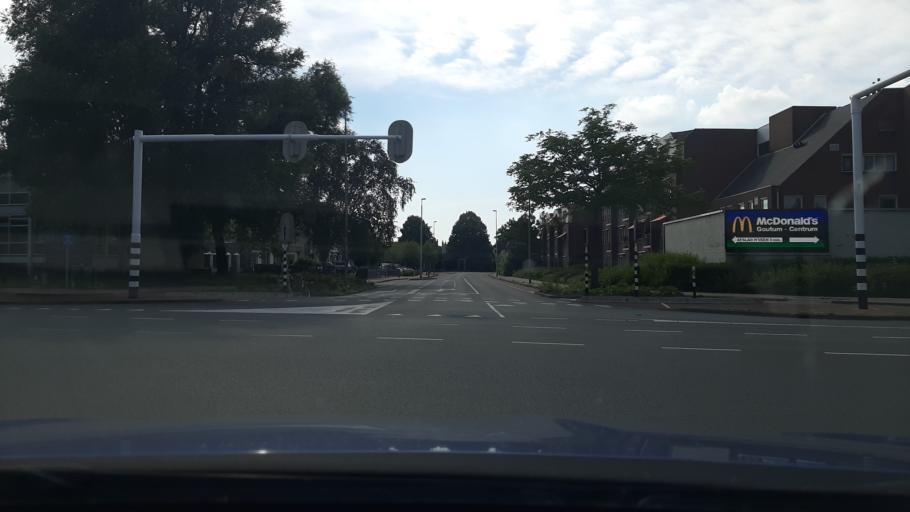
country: NL
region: Friesland
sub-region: Gemeente Leeuwarden
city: Huizum
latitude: 53.1910
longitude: 5.8002
